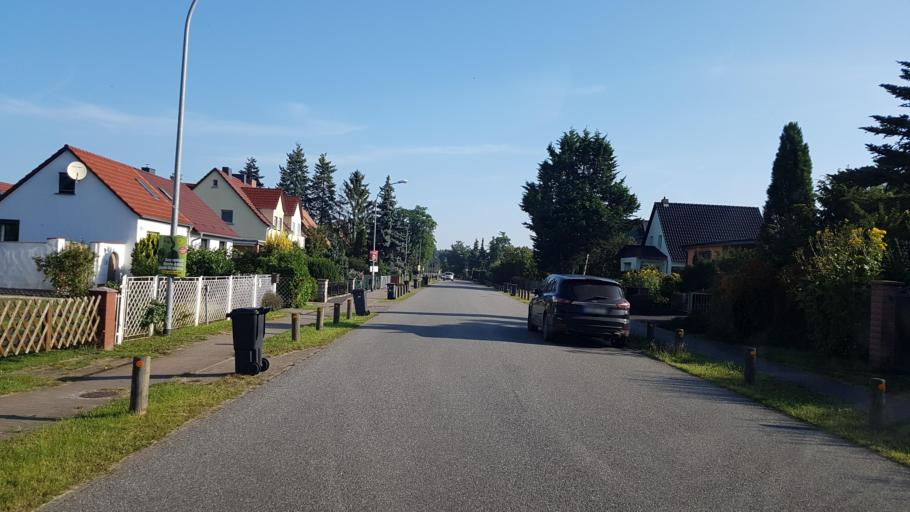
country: DE
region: Brandenburg
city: Brandenburg an der Havel
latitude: 52.4299
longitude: 12.5783
